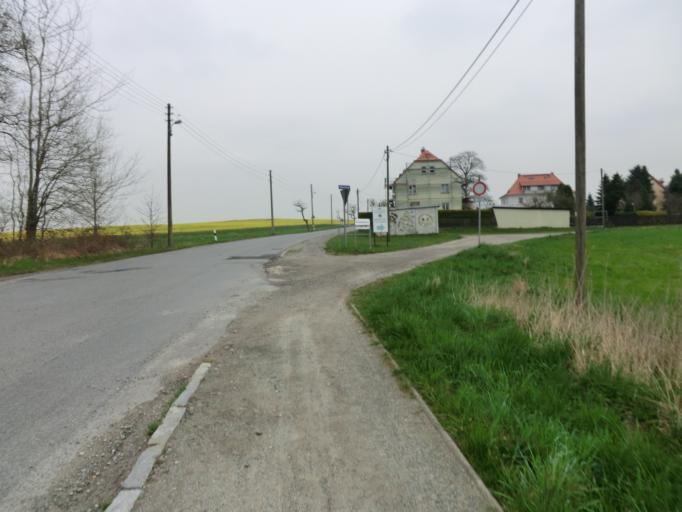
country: DE
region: Saxony
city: Ottendorf-Okrilla
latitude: 51.1301
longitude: 13.8504
